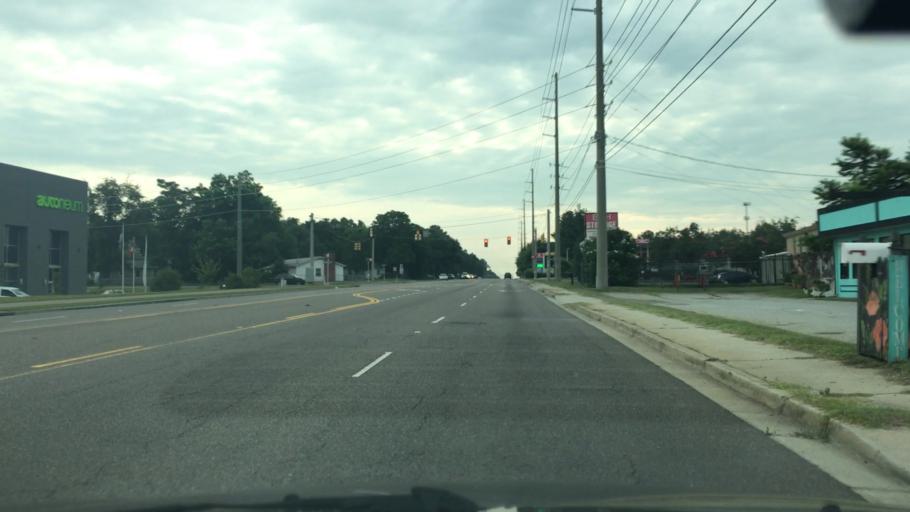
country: US
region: South Carolina
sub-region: Aiken County
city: Aiken
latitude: 33.5300
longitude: -81.7038
